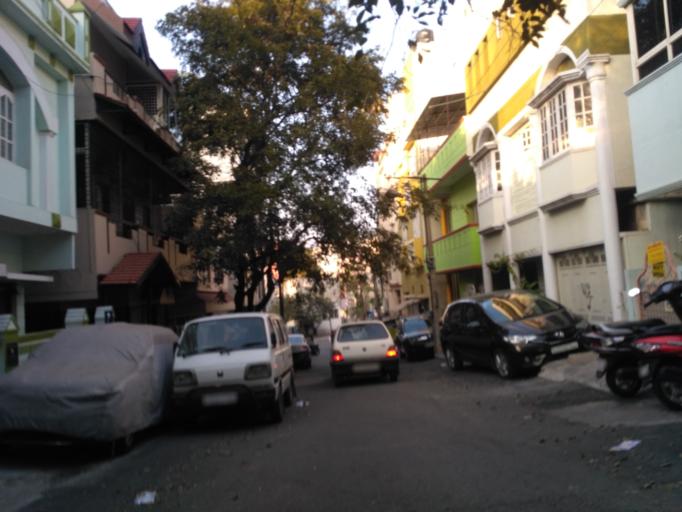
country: IN
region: Karnataka
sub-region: Bangalore Urban
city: Bangalore
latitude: 12.9601
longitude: 77.5291
